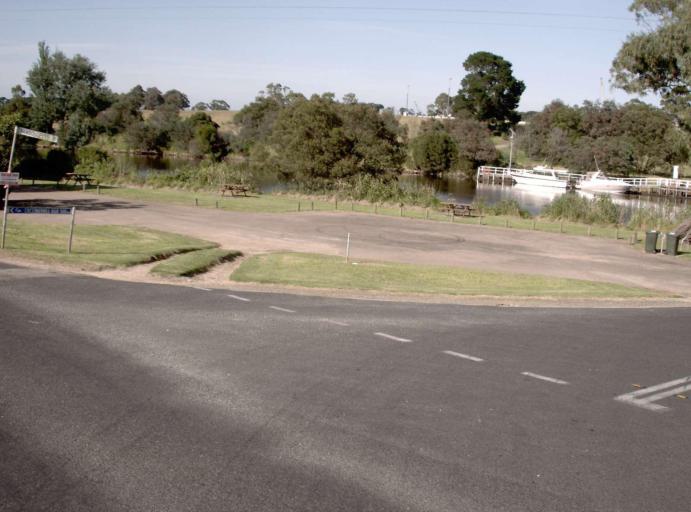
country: AU
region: Victoria
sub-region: East Gippsland
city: Lakes Entrance
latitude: -37.8225
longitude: 147.8637
